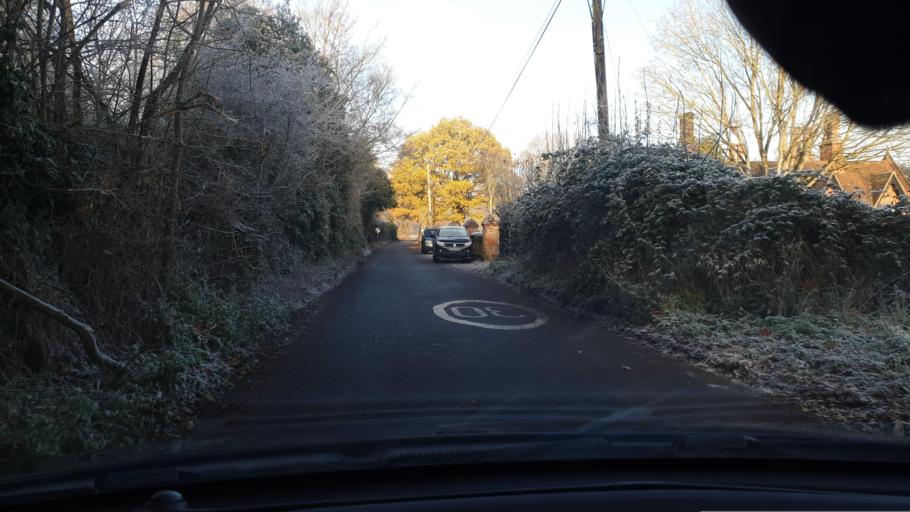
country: GB
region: England
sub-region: Essex
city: Mistley
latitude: 51.9718
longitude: 1.1234
